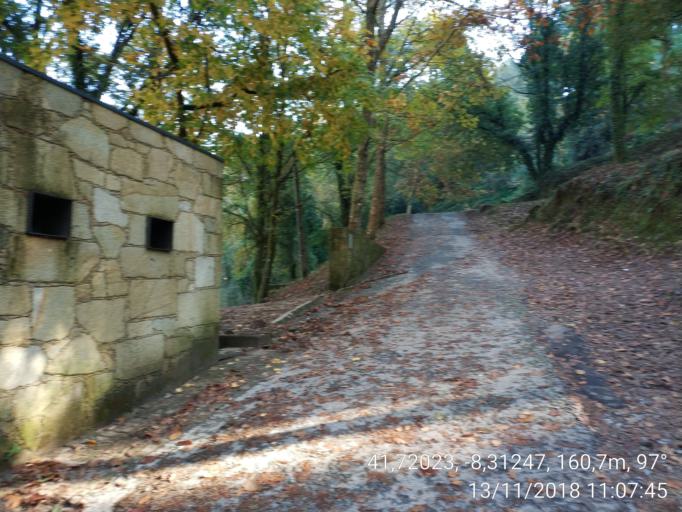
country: PT
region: Braga
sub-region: Terras de Bouro
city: Terras de Bouro
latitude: 41.7202
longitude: -8.3125
